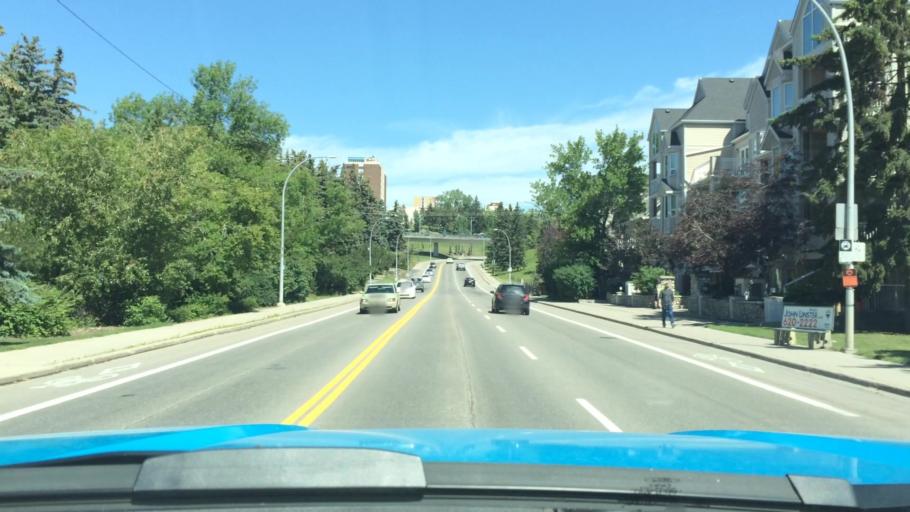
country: CA
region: Alberta
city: Calgary
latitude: 51.0586
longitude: -114.0860
